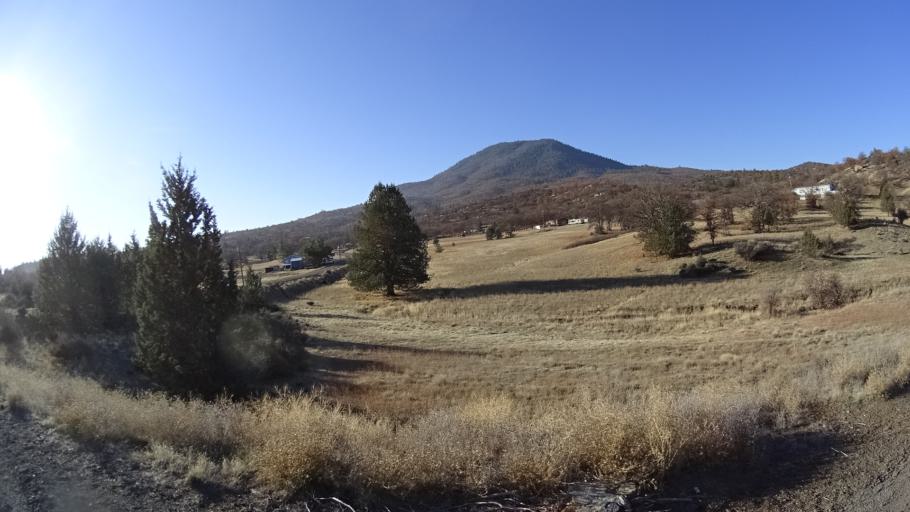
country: US
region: California
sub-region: Siskiyou County
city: Montague
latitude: 41.8916
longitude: -122.4914
